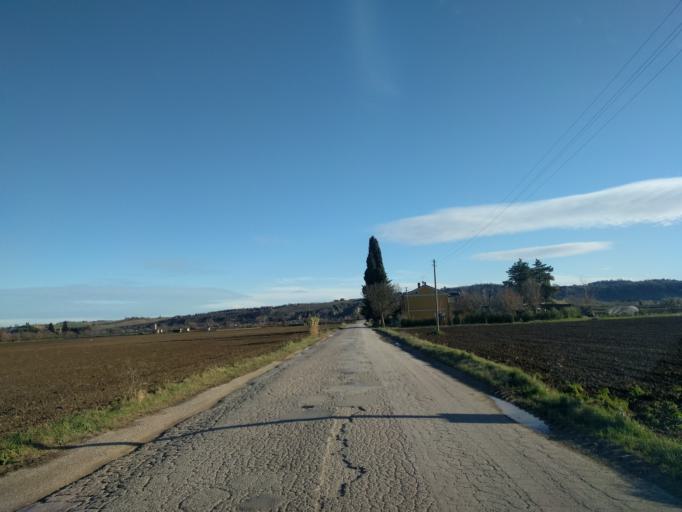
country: IT
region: The Marches
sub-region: Provincia di Pesaro e Urbino
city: Cuccurano
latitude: 43.7811
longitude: 12.9777
